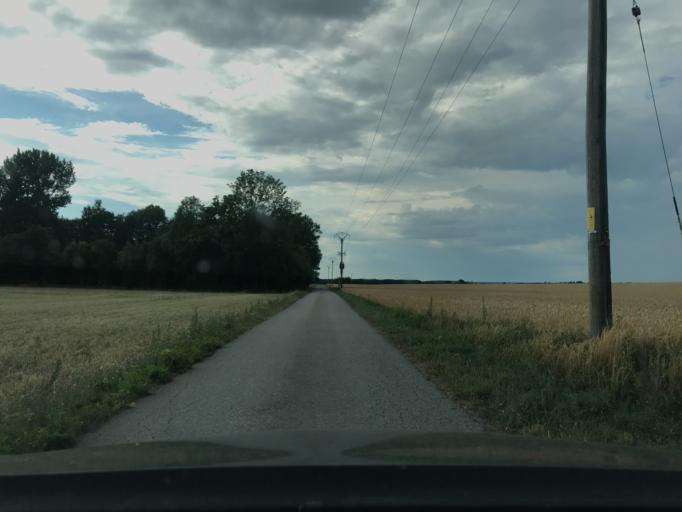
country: SE
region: Skane
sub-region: Simrishamns Kommun
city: Kivik
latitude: 55.5294
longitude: 14.1616
